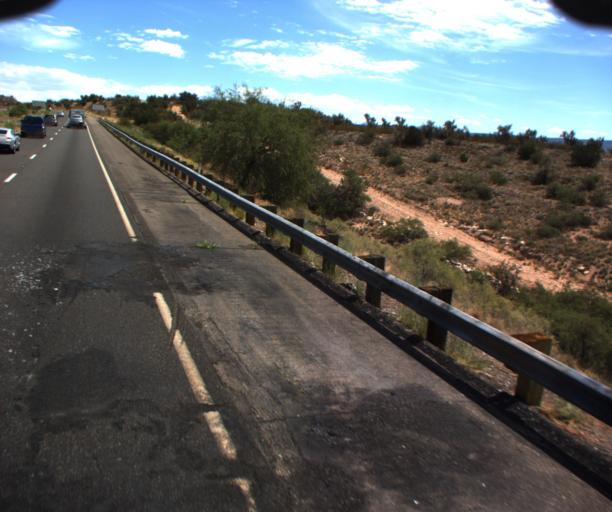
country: US
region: Arizona
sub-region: Yavapai County
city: Lake Montezuma
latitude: 34.6528
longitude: -111.7963
